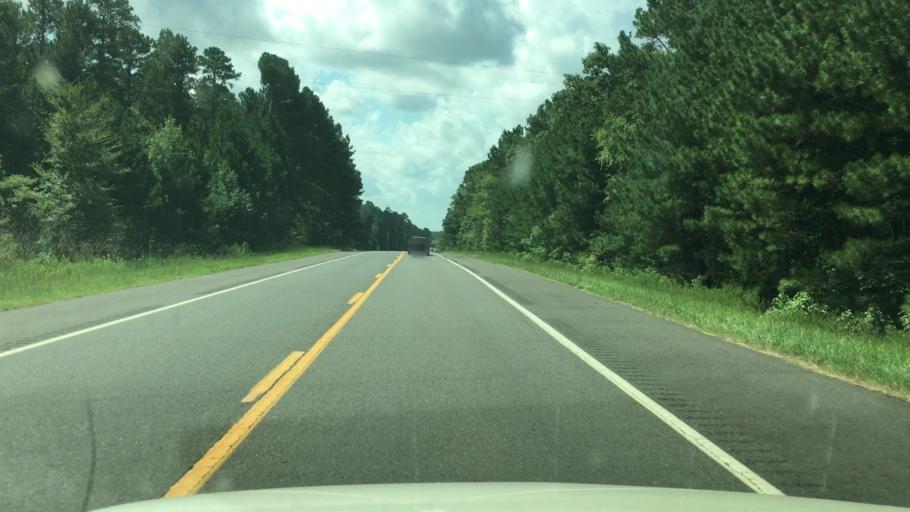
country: US
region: Arkansas
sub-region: Clark County
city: Arkadelphia
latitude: 34.1976
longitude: -93.0764
